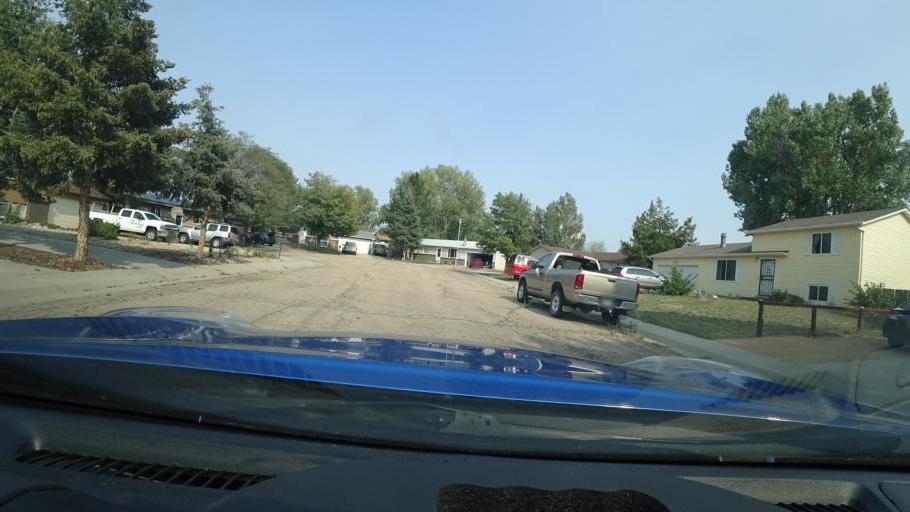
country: US
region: Colorado
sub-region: Adams County
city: Aurora
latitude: 39.6670
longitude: -104.8047
